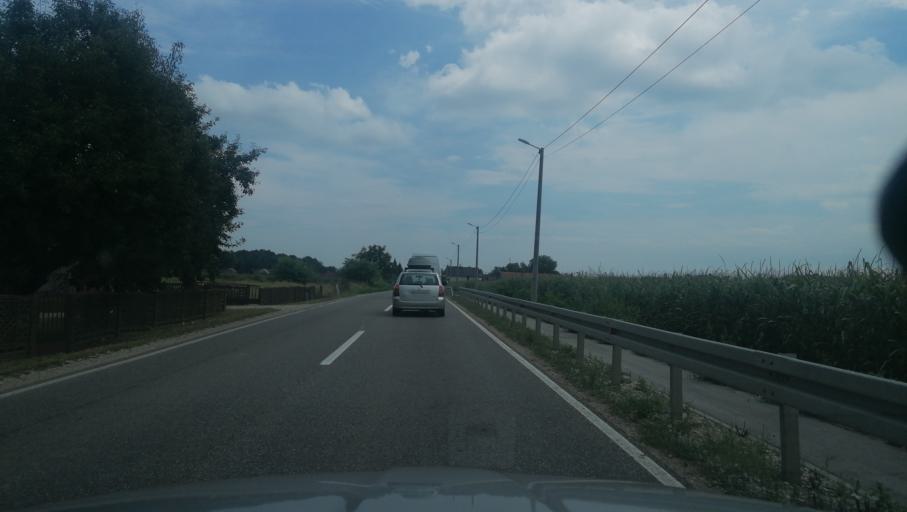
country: BA
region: Republika Srpska
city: Obudovac
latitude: 44.9570
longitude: 18.6331
